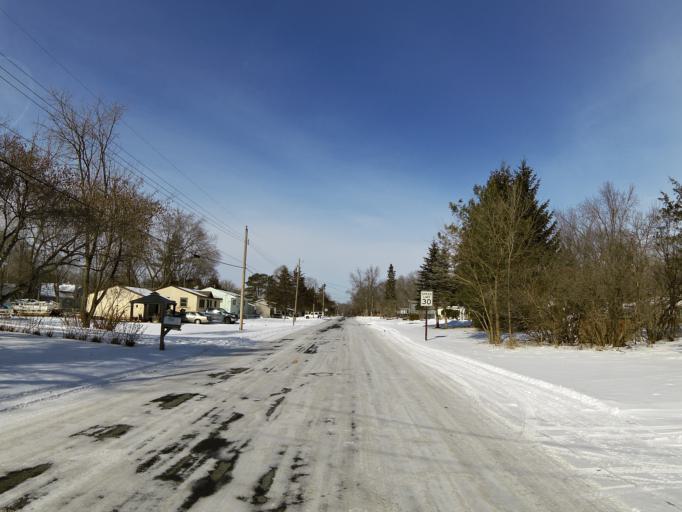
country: US
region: Minnesota
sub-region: Washington County
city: Lake Saint Croix Beach
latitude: 44.9256
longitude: -92.7686
